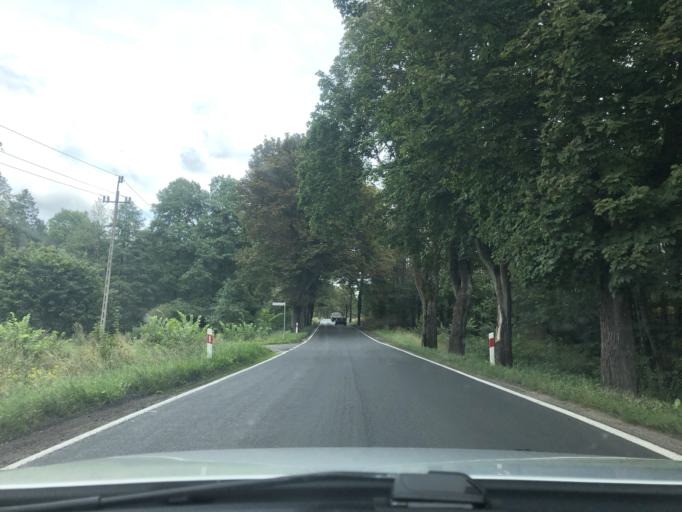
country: PL
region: Greater Poland Voivodeship
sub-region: Powiat czarnkowsko-trzcianecki
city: Wielen
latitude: 52.9023
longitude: 16.1067
